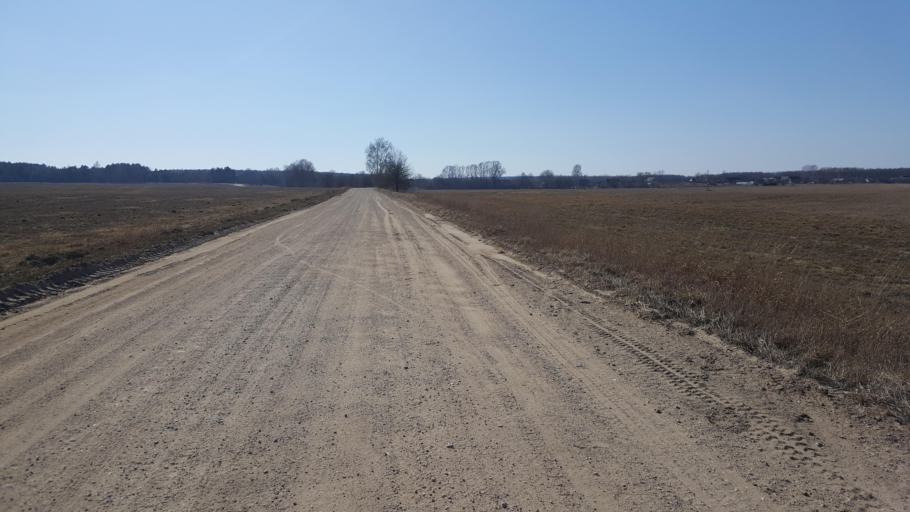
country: BY
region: Brest
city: Kamyanyets
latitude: 52.3576
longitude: 23.7610
